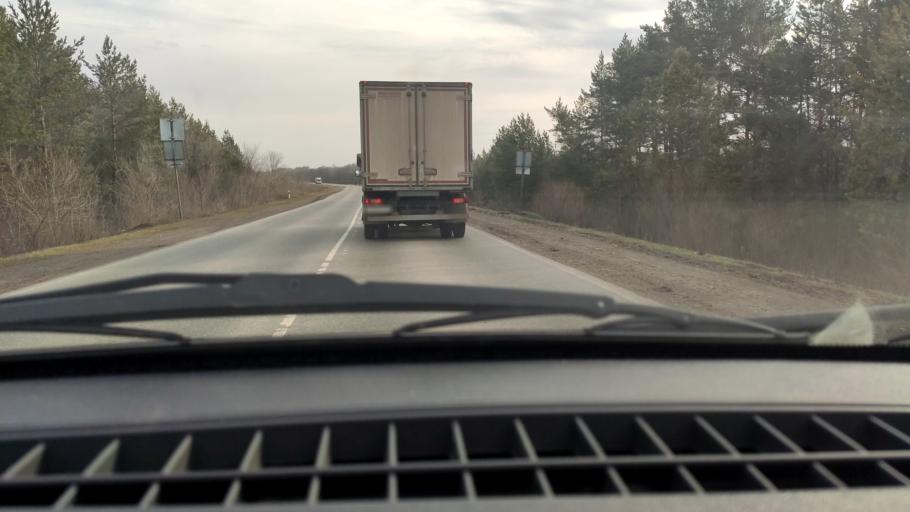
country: RU
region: Bashkortostan
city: Davlekanovo
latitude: 54.2458
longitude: 55.0753
